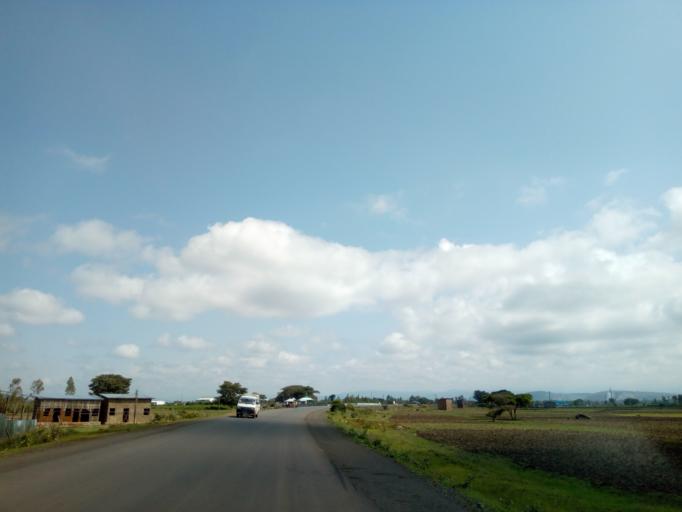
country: ET
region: Oromiya
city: Waliso
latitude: 8.5469
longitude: 37.9582
